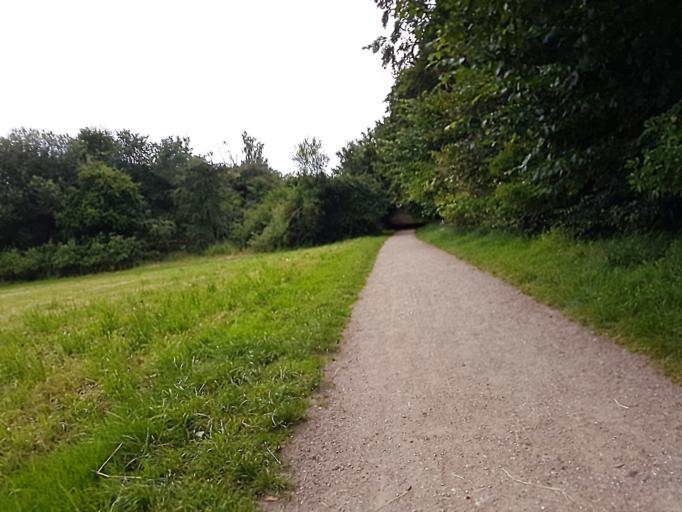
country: DK
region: Capital Region
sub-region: Fureso Kommune
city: Vaerlose
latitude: 55.7920
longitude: 12.3592
